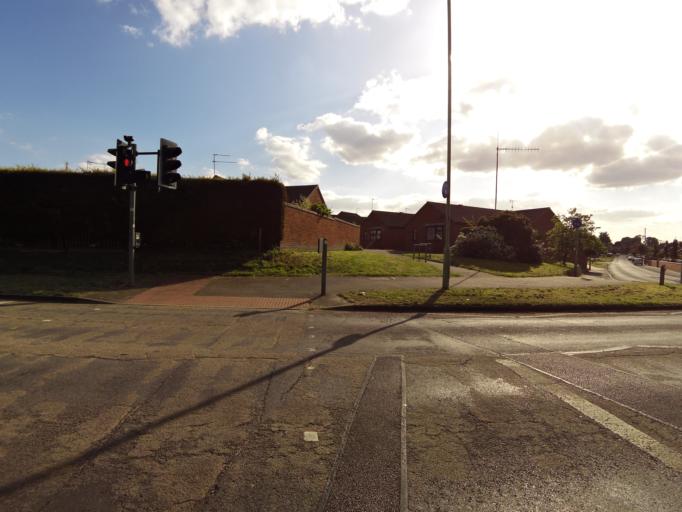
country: GB
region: England
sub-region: Suffolk
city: Beccles
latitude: 52.4484
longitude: 1.5839
